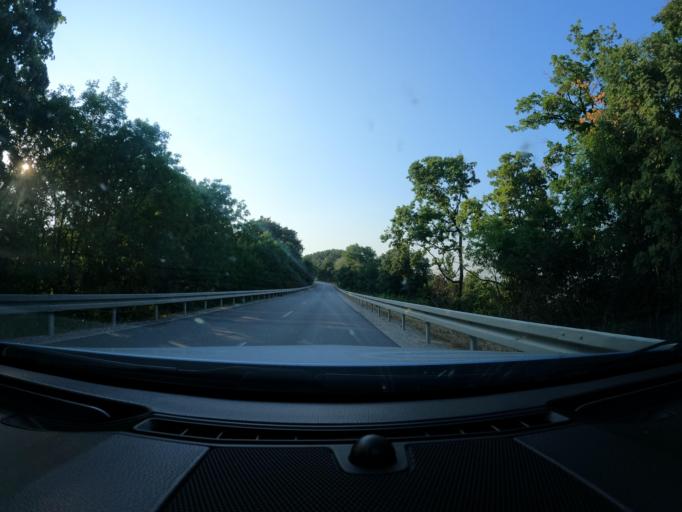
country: RS
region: Autonomna Pokrajina Vojvodina
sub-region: Juznobacki Okrug
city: Beocin
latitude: 45.1657
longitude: 19.7134
